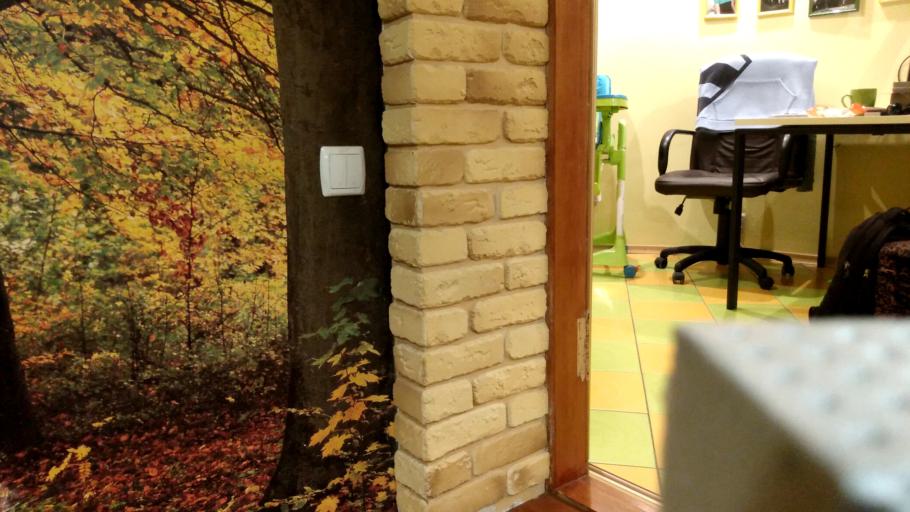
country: RU
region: Republic of Karelia
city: Pudozh
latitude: 61.8046
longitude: 37.6701
